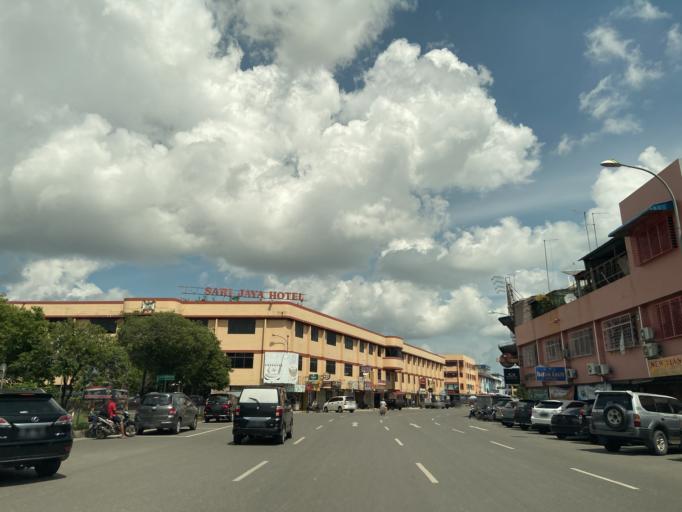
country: SG
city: Singapore
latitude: 1.1478
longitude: 104.0094
